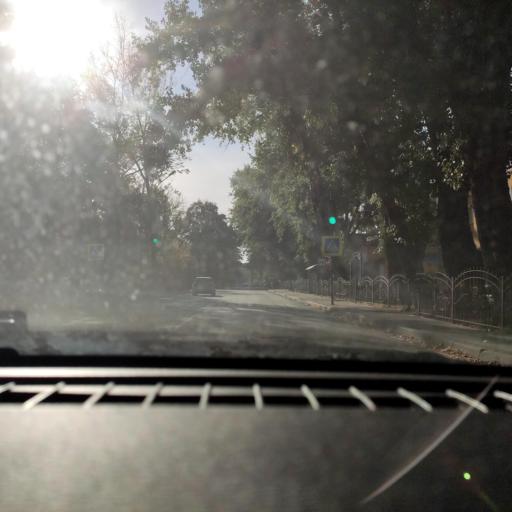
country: RU
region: Voronezj
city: Voronezh
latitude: 51.7163
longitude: 39.2221
